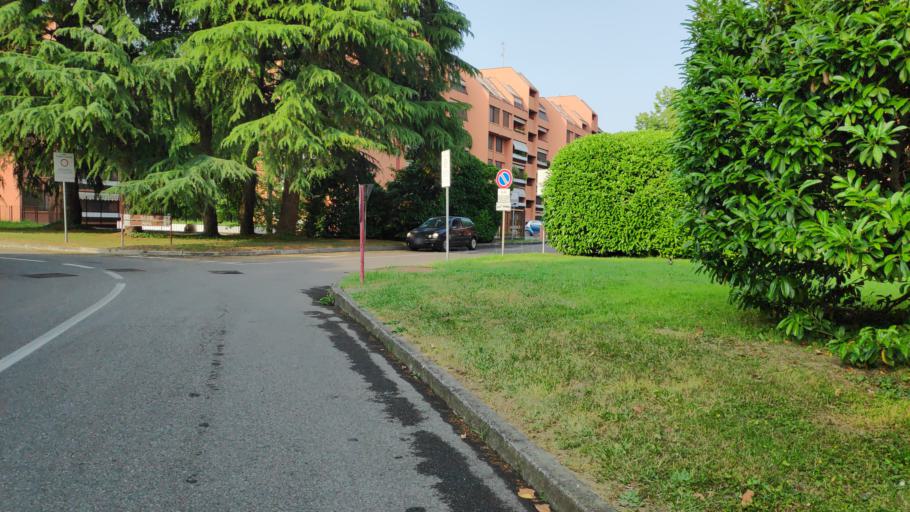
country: IT
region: Lombardy
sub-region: Citta metropolitana di Milano
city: Basiglio
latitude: 45.3623
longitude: 9.1636
